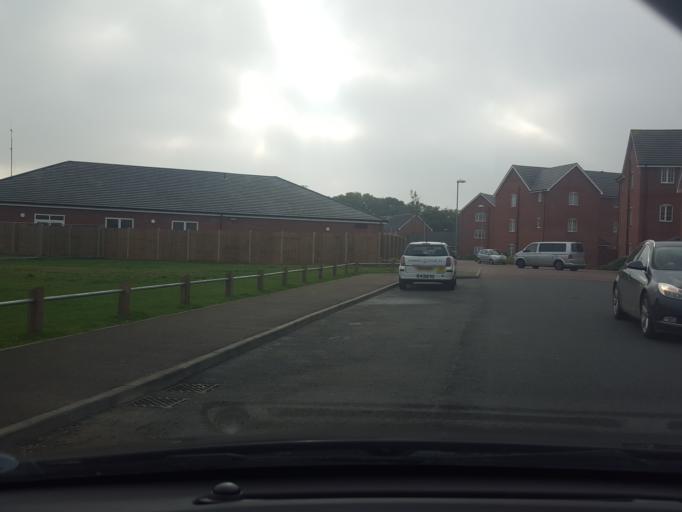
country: GB
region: England
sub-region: Essex
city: Little Clacton
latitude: 51.8040
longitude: 1.1232
